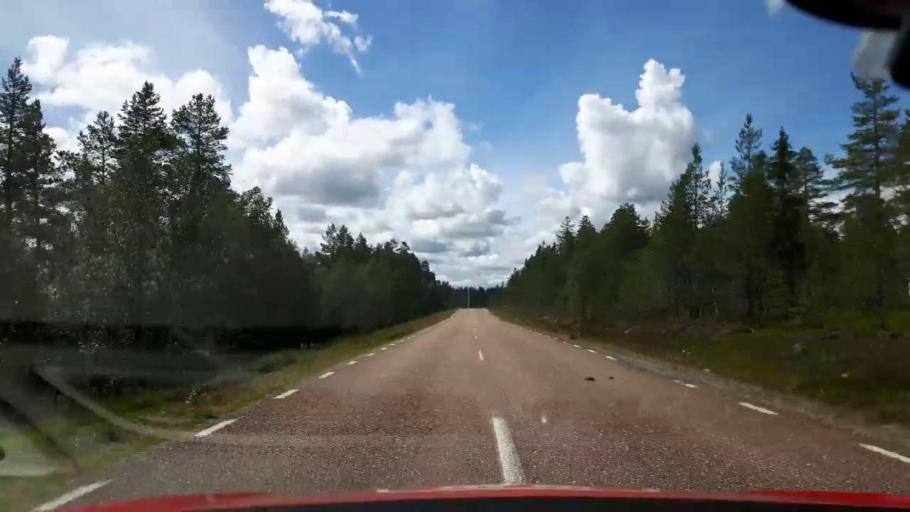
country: SE
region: Dalarna
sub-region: Alvdalens Kommun
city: AElvdalen
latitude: 61.8078
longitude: 13.5204
